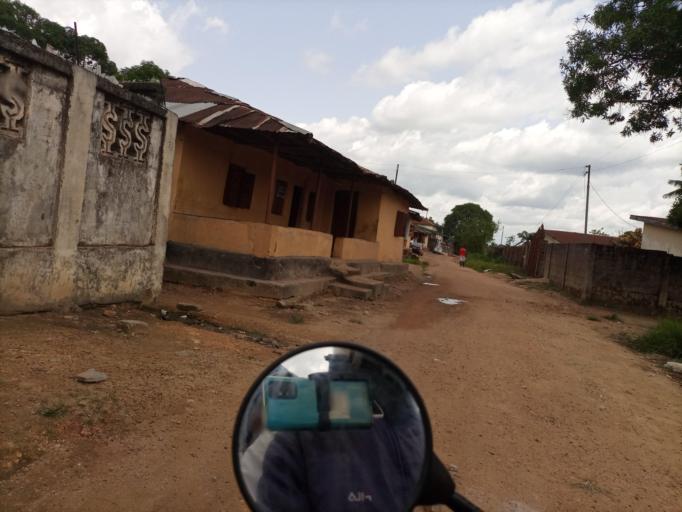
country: SL
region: Southern Province
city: Bo
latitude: 7.9512
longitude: -11.7340
